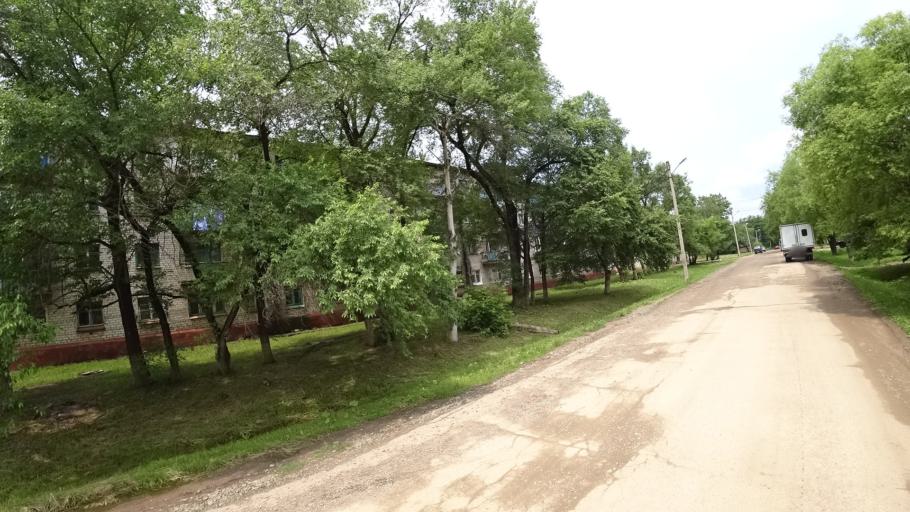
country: RU
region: Primorskiy
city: Novosysoyevka
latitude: 44.2276
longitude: 133.3614
